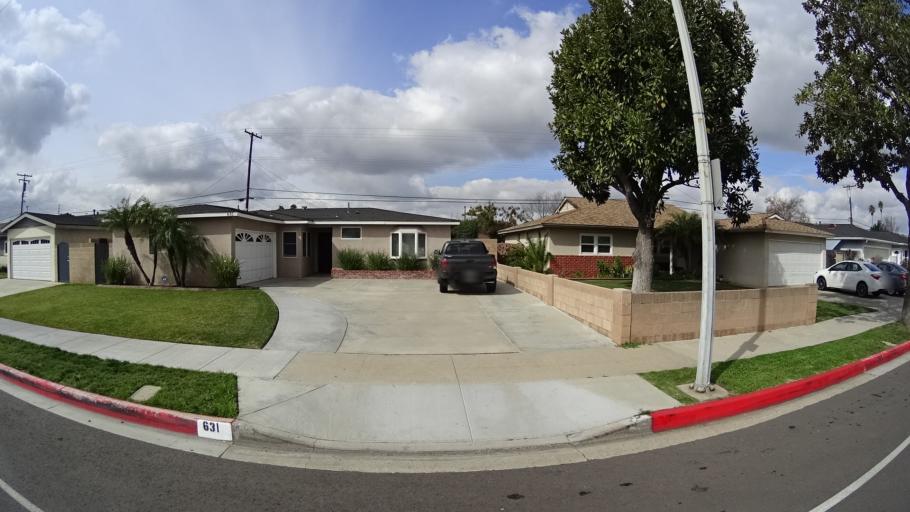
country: US
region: California
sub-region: Orange County
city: Buena Park
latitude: 33.8413
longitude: -117.9678
